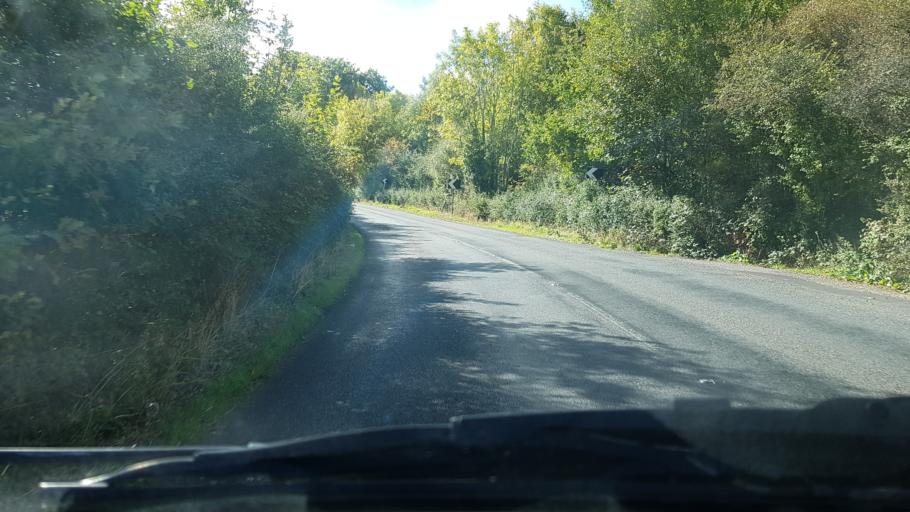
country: GB
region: England
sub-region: West Sussex
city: Billingshurst
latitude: 51.0099
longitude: -0.4761
